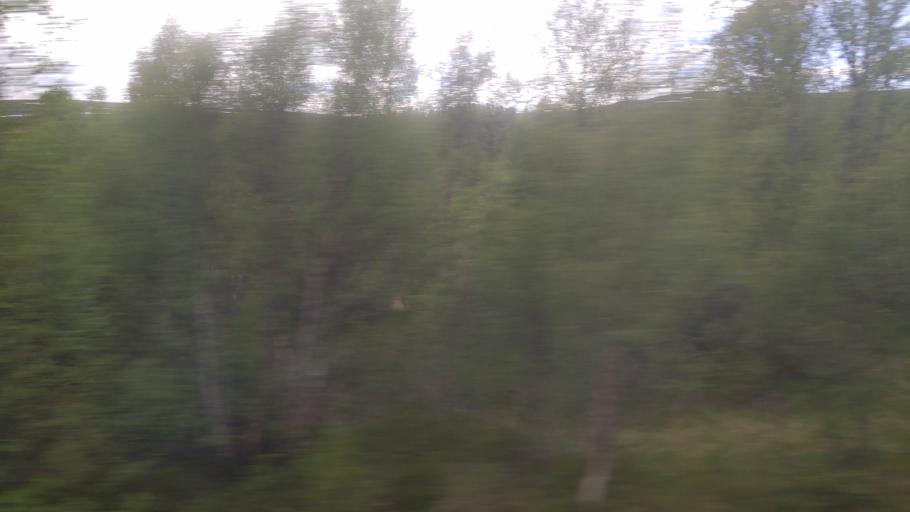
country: NO
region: Sor-Trondelag
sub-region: Holtalen
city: Alen
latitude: 62.7495
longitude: 11.3295
